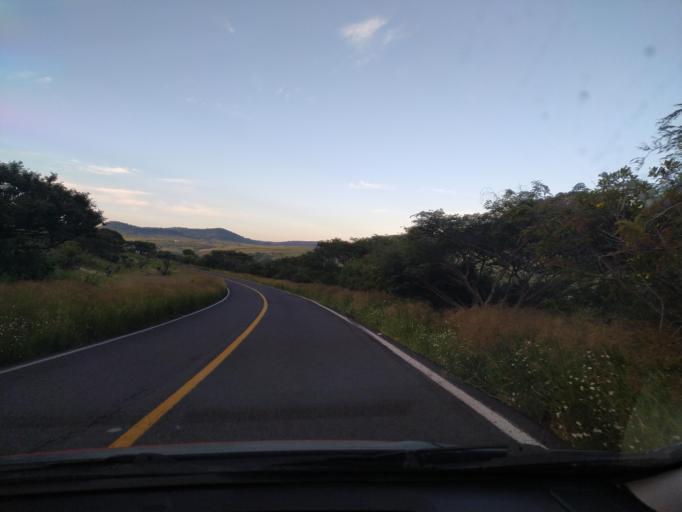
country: MX
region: Guanajuato
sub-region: Penjamo
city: Estacion la Piedad
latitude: 20.5250
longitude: -101.9736
